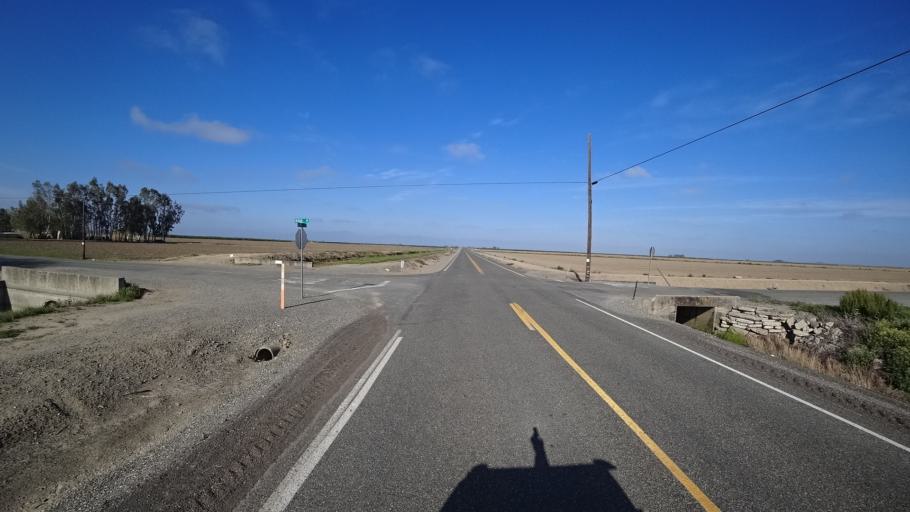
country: US
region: California
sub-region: Glenn County
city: Willows
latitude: 39.5821
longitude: -122.1168
